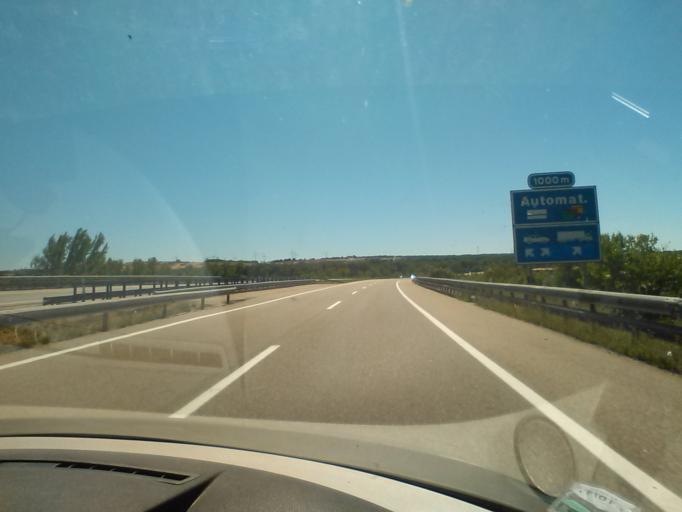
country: ES
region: Castille and Leon
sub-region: Provincia de Burgos
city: Cardenajimeno
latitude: 42.3415
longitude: -3.6082
